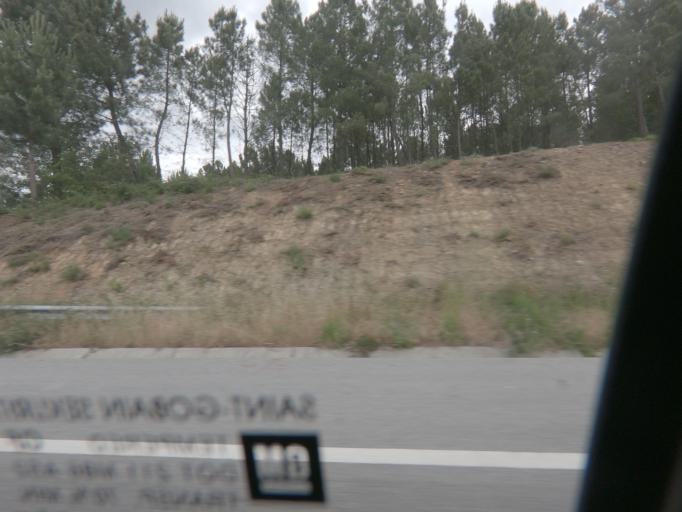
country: PT
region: Vila Real
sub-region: Sabrosa
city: Vilela
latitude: 41.2644
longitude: -7.6608
